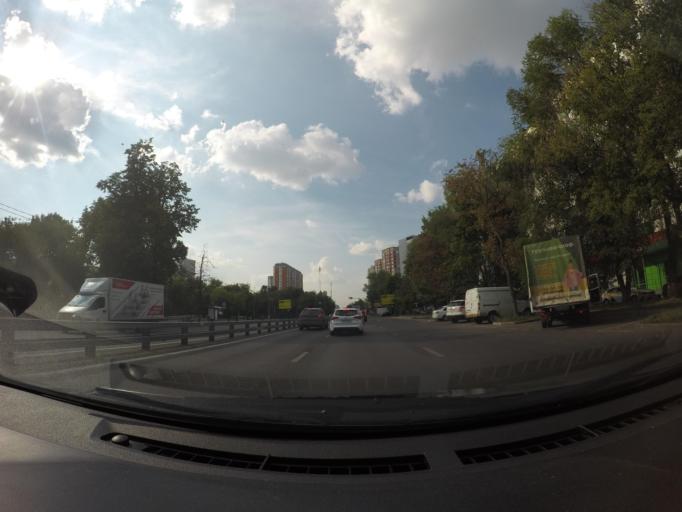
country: RU
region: Moscow
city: Zhulebino
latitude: 55.6957
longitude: 37.8618
